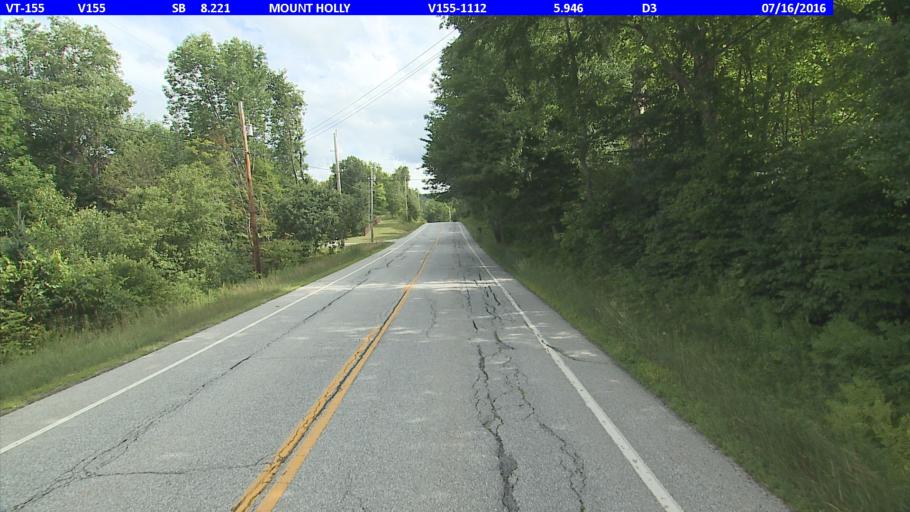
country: US
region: Vermont
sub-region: Rutland County
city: Rutland
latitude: 43.4285
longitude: -72.8576
